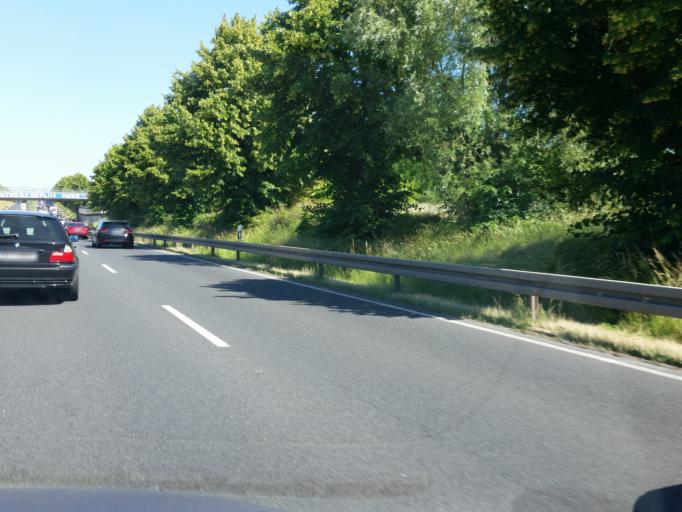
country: DE
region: Berlin
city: Lichtenrade
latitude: 52.3673
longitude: 13.4034
